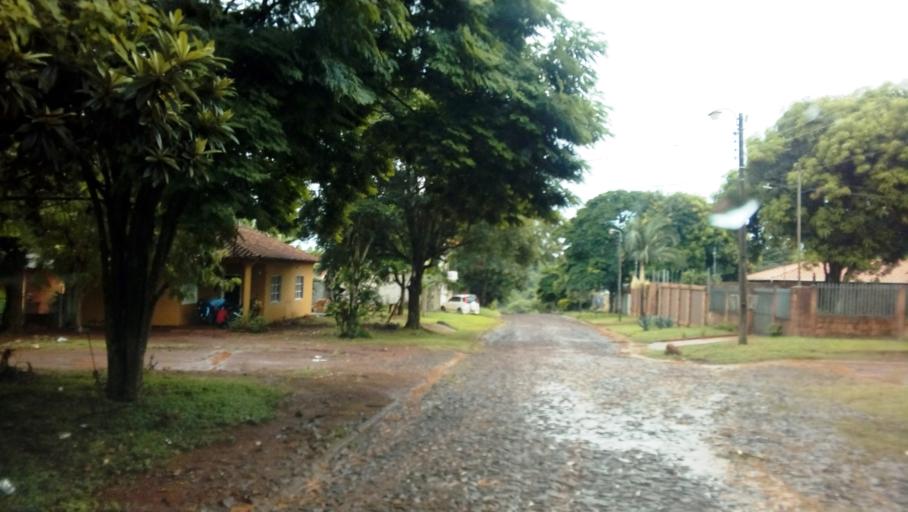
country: PY
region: Alto Parana
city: Ciudad del Este
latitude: -25.4193
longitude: -54.6384
